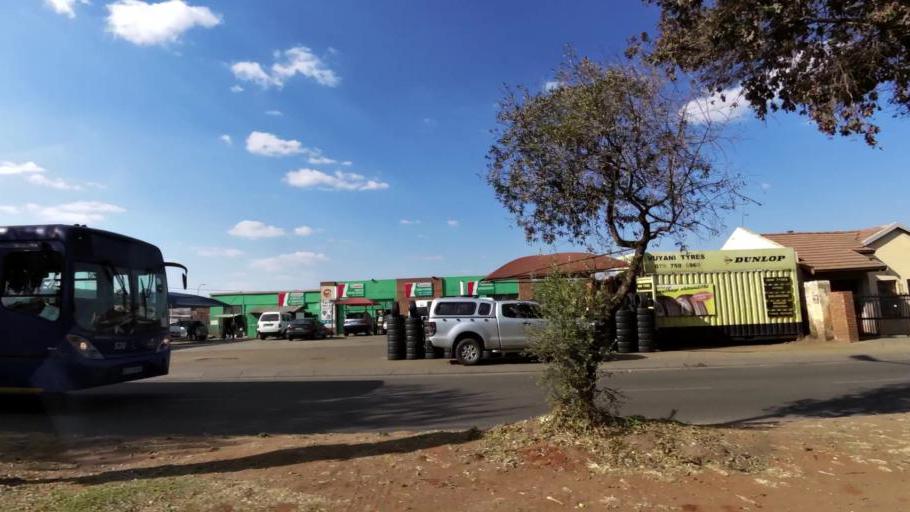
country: ZA
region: Gauteng
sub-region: City of Johannesburg Metropolitan Municipality
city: Soweto
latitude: -26.2171
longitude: 27.8713
